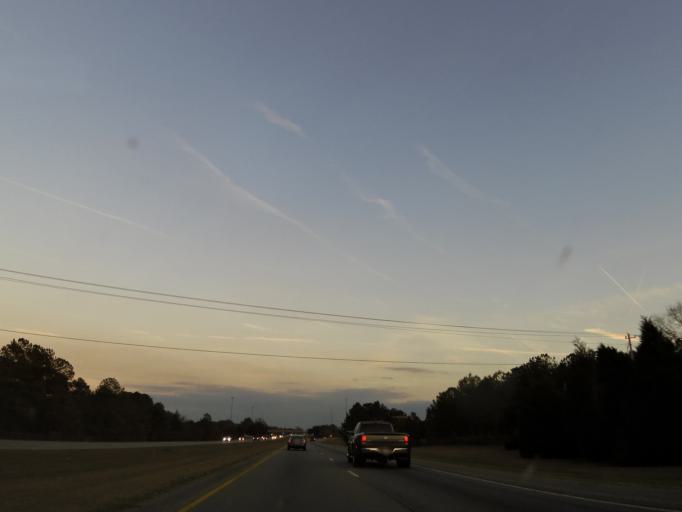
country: US
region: Georgia
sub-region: Dougherty County
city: Albany
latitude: 31.5937
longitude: -84.1316
